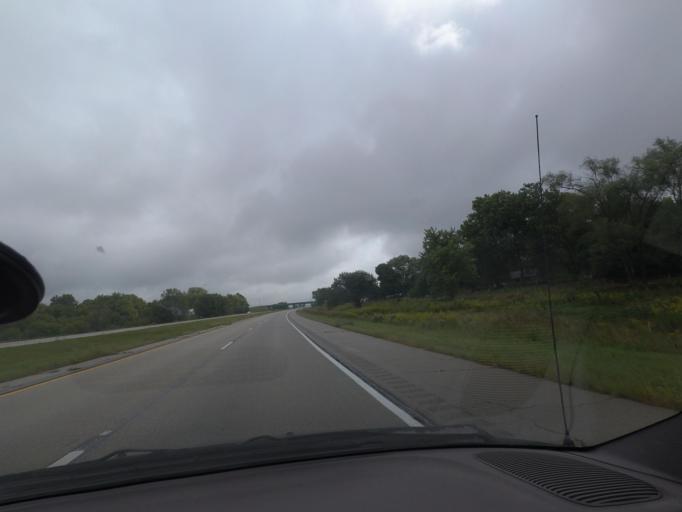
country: US
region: Illinois
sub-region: Piatt County
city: Monticello
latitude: 40.0517
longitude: -88.5708
